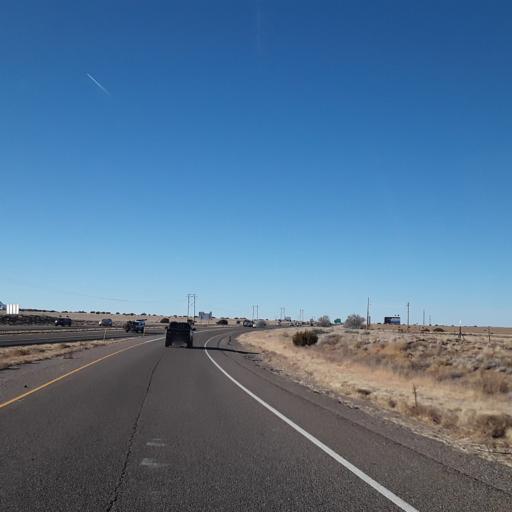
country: US
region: New Mexico
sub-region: Sandoval County
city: Santo Domingo Pueblo
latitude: 35.4704
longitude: -106.3057
